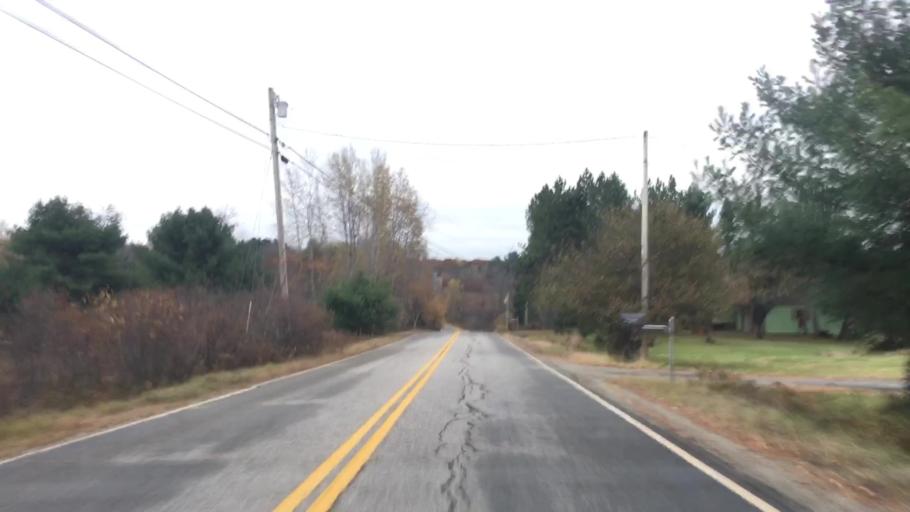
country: US
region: Maine
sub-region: Lincoln County
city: Whitefield
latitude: 44.1688
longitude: -69.6586
